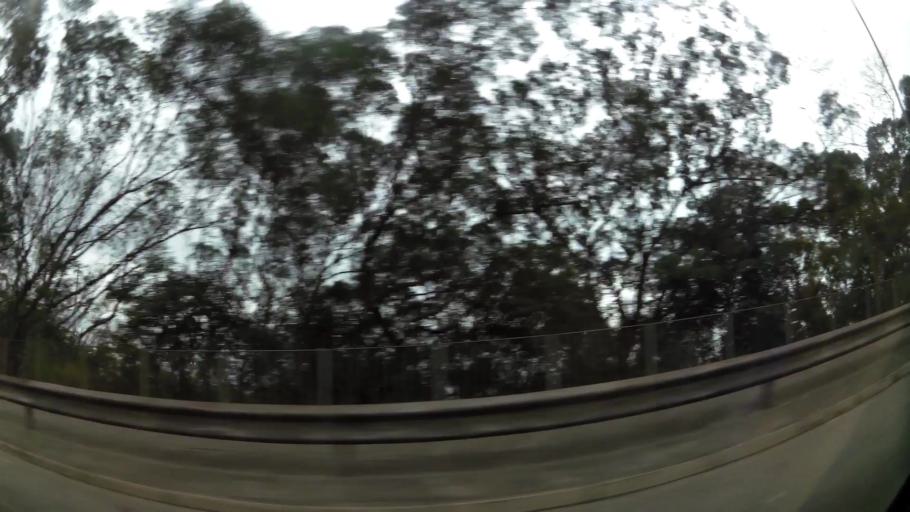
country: HK
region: Tsuen Wan
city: Tsuen Wan
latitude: 22.3291
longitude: 114.0944
